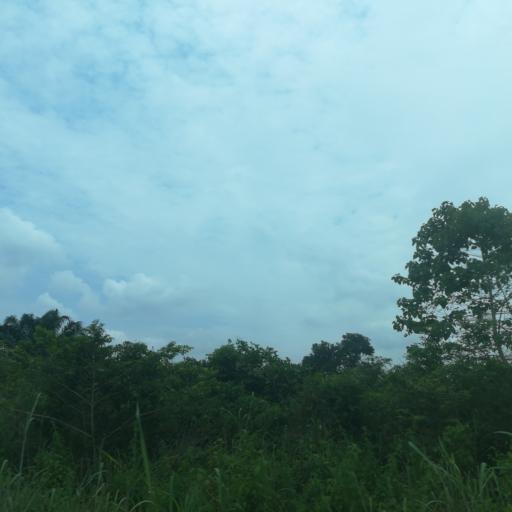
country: NG
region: Lagos
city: Ejirin
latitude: 6.6521
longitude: 3.8260
